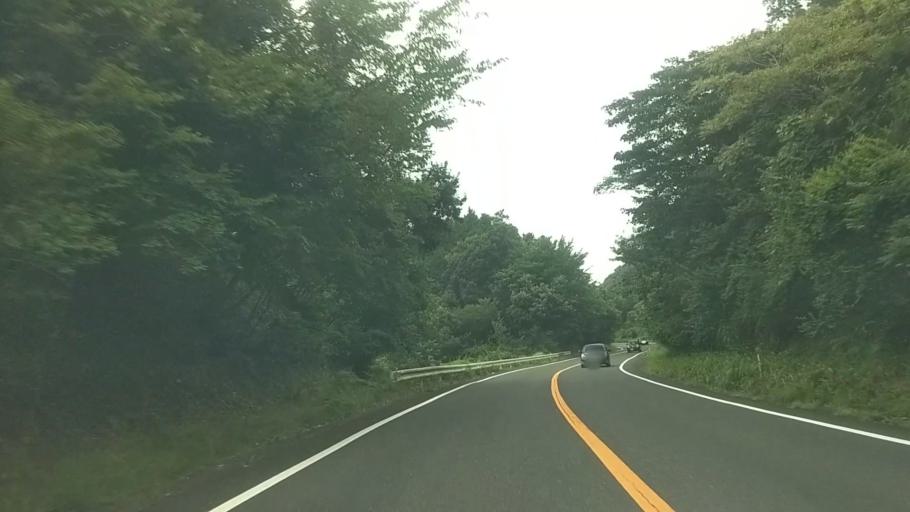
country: JP
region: Chiba
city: Kawaguchi
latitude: 35.2143
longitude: 140.0499
